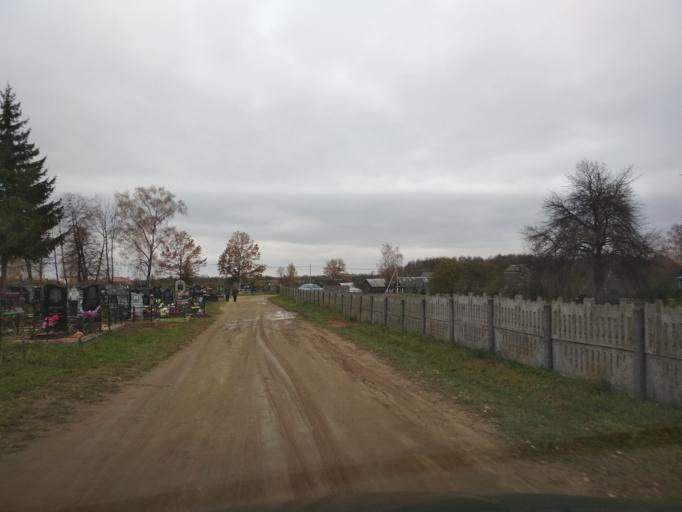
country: BY
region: Minsk
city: Blon'
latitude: 53.5210
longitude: 28.1798
